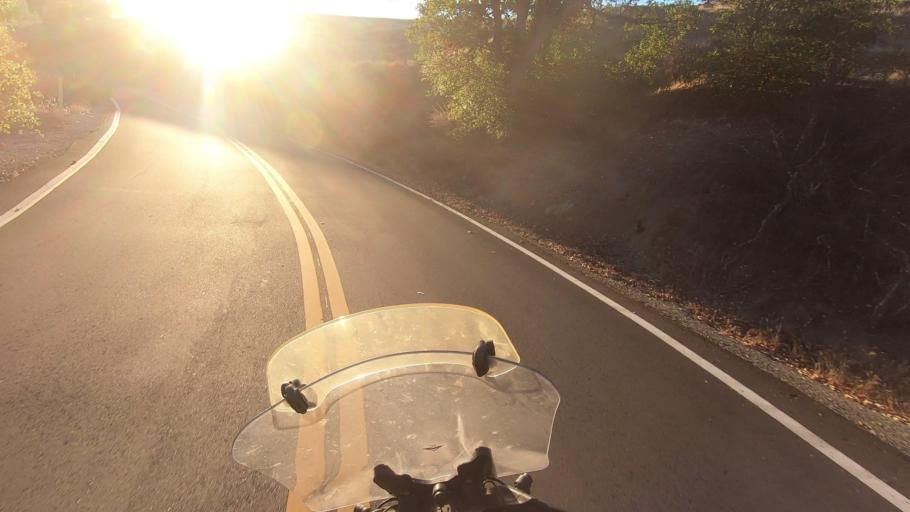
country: US
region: California
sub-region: Santa Clara County
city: East Foothills
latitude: 37.3347
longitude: -121.7027
